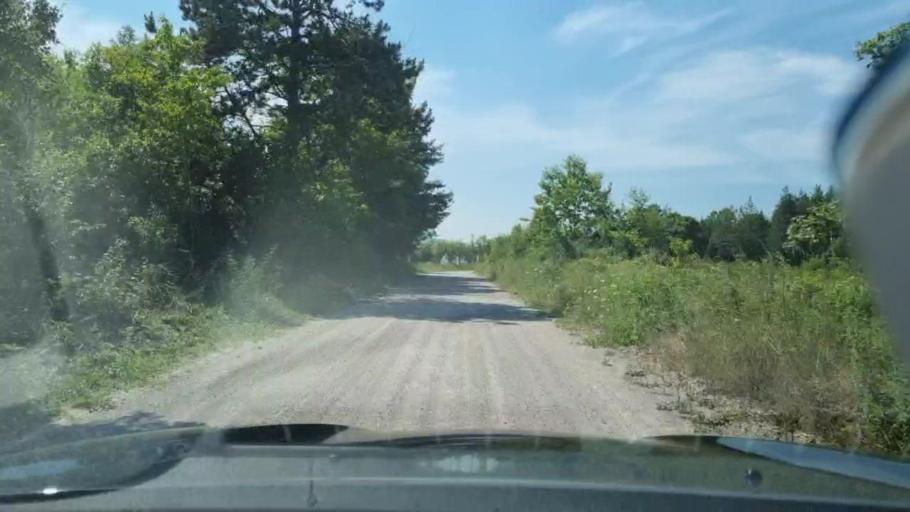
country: BA
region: Federation of Bosnia and Herzegovina
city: Orasac
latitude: 44.6337
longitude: 16.2768
